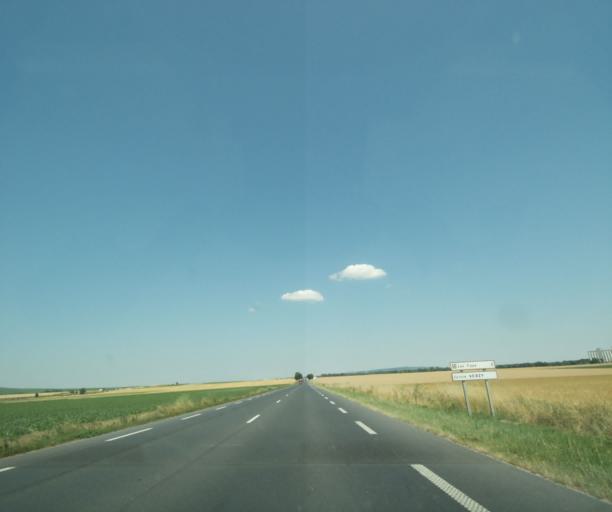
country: FR
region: Champagne-Ardenne
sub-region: Departement de la Marne
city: Verzy
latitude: 49.1500
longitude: 4.2134
